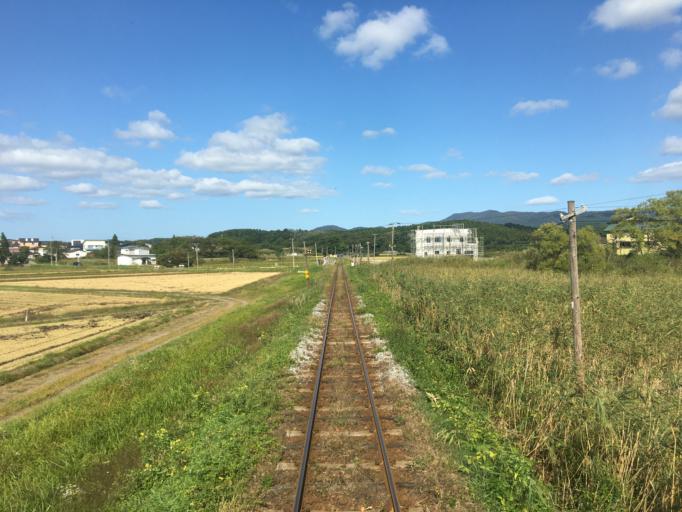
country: JP
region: Aomori
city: Goshogawara
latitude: 40.9496
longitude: 140.4394
